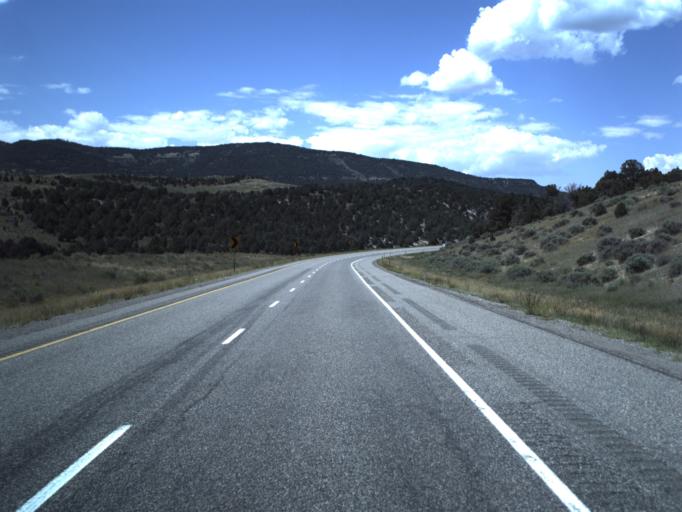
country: US
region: Utah
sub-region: Sevier County
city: Salina
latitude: 38.8515
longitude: -111.5443
